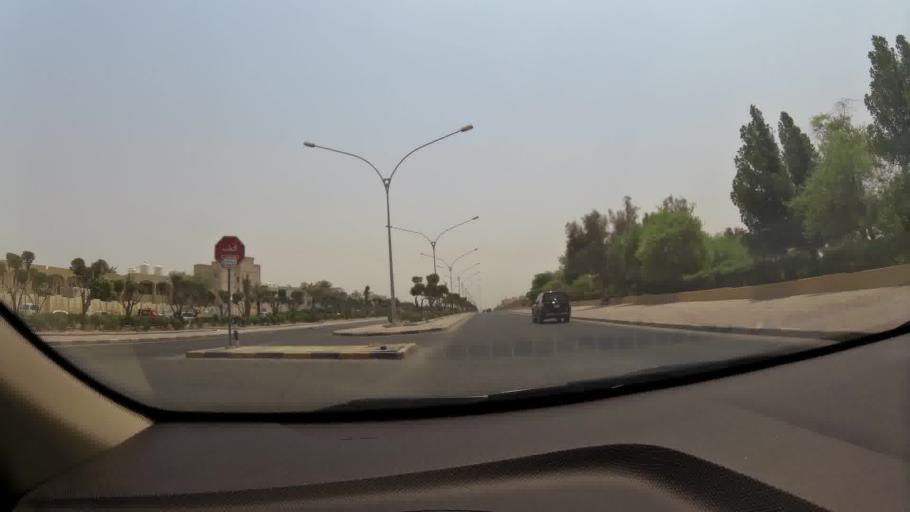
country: KW
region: Al Asimah
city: Ar Rabiyah
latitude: 29.3170
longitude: 47.8190
